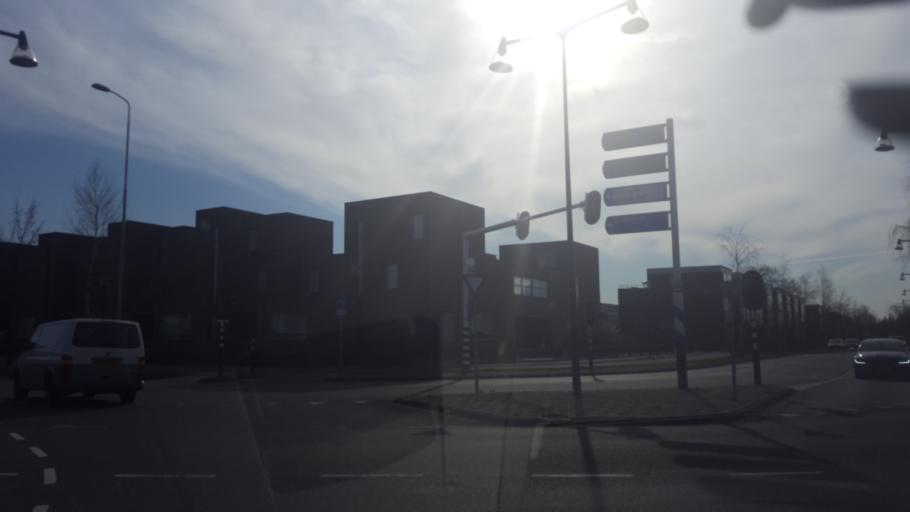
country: NL
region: North Brabant
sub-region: Gemeente Eindhoven
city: Meerhoven
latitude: 51.4360
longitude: 5.4157
